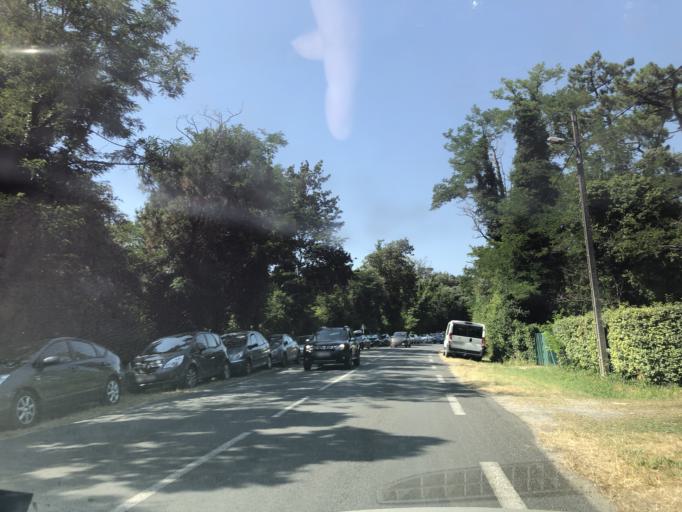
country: FR
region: Poitou-Charentes
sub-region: Departement de la Charente-Maritime
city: Meschers-sur-Gironde
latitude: 45.5670
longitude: -0.9710
